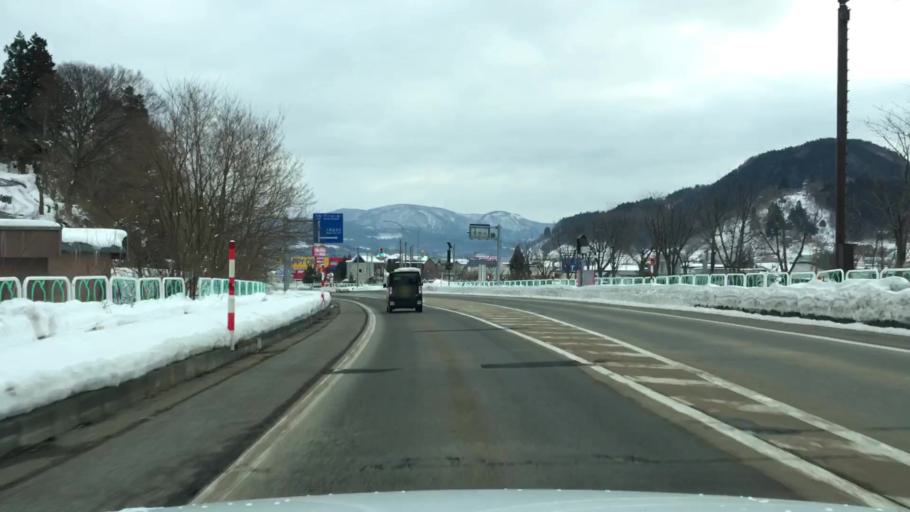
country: JP
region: Aomori
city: Hirosaki
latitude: 40.5237
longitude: 140.5637
